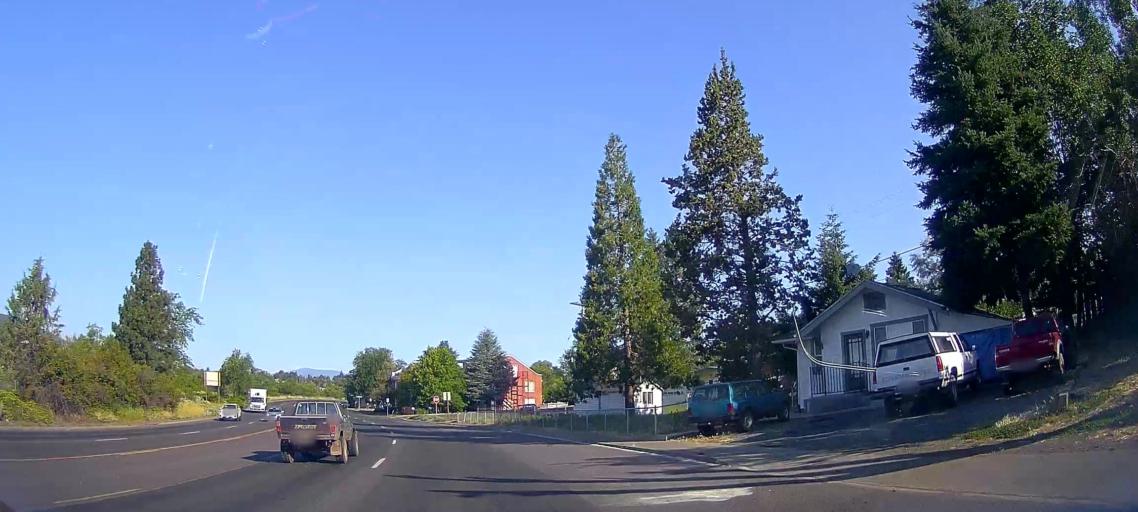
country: US
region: Oregon
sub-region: Klamath County
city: Klamath Falls
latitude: 42.2294
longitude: -121.7673
